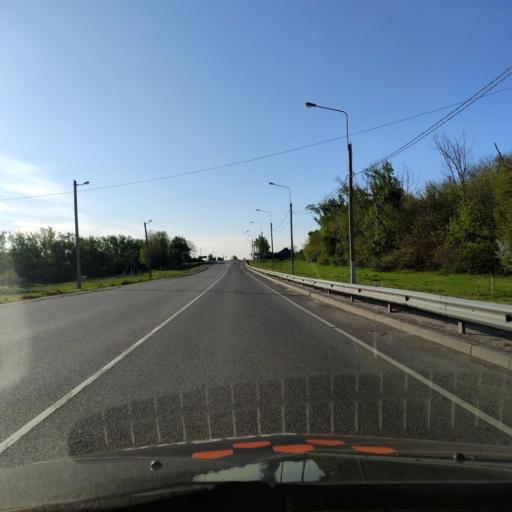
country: RU
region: Lipetsk
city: Yelets
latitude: 52.5565
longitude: 38.6970
